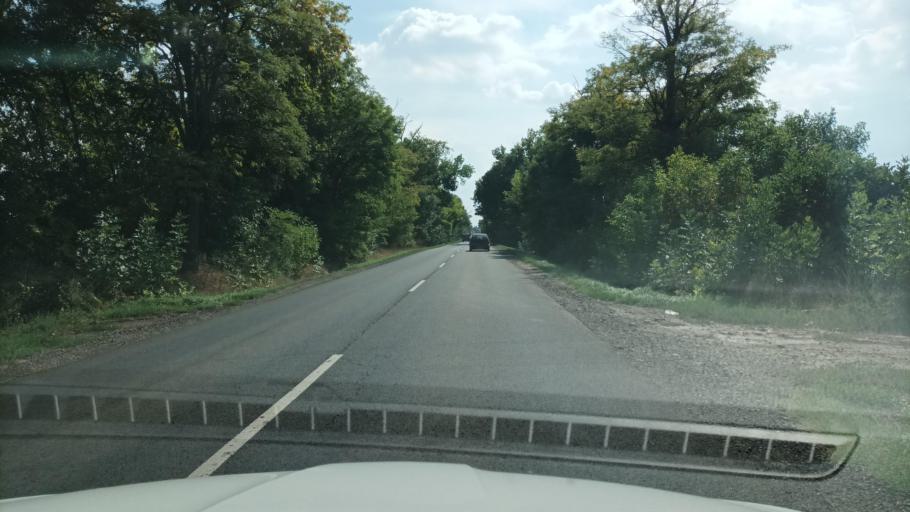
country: HU
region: Pest
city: Zsambok
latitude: 47.5591
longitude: 19.6040
